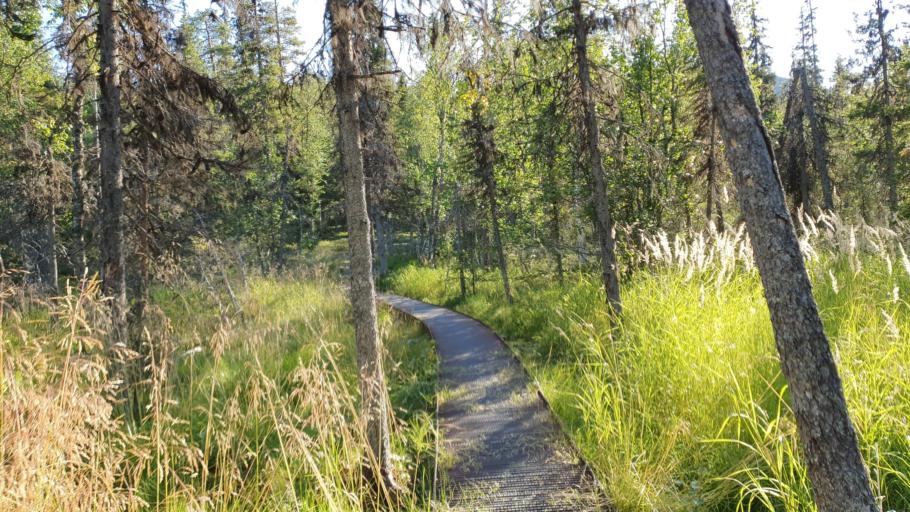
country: FI
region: Lapland
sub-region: Tunturi-Lappi
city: Kolari
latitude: 67.5967
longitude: 24.2543
